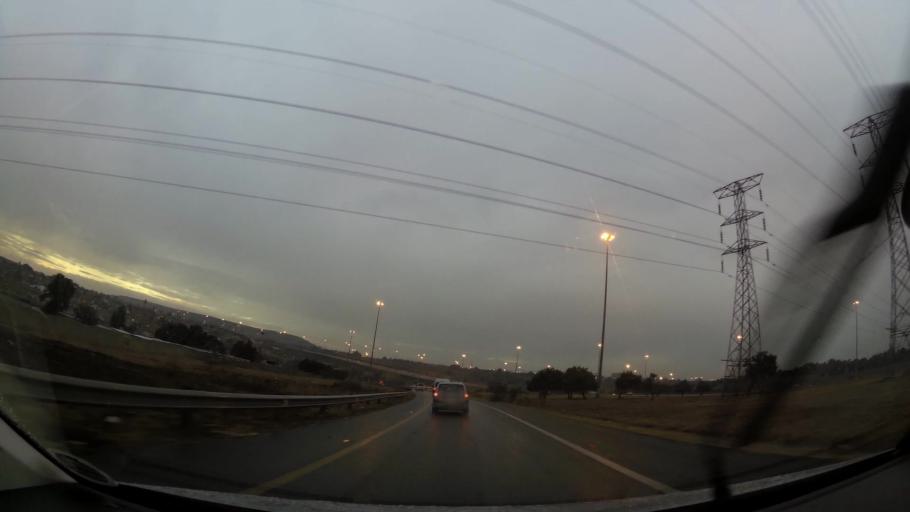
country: ZA
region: Gauteng
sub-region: City of Johannesburg Metropolitan Municipality
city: Soweto
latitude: -26.2617
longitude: 27.9570
